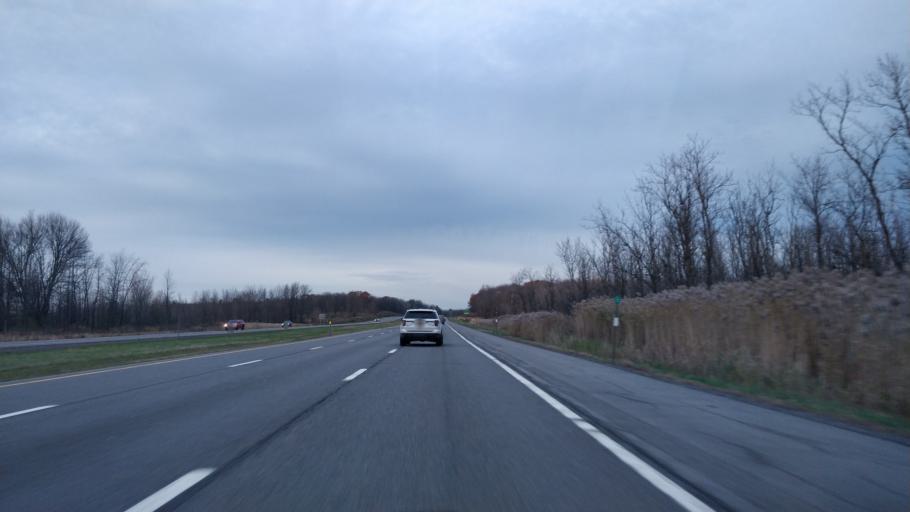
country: US
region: New York
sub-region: Onondaga County
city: Brewerton
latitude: 43.2618
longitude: -76.1308
